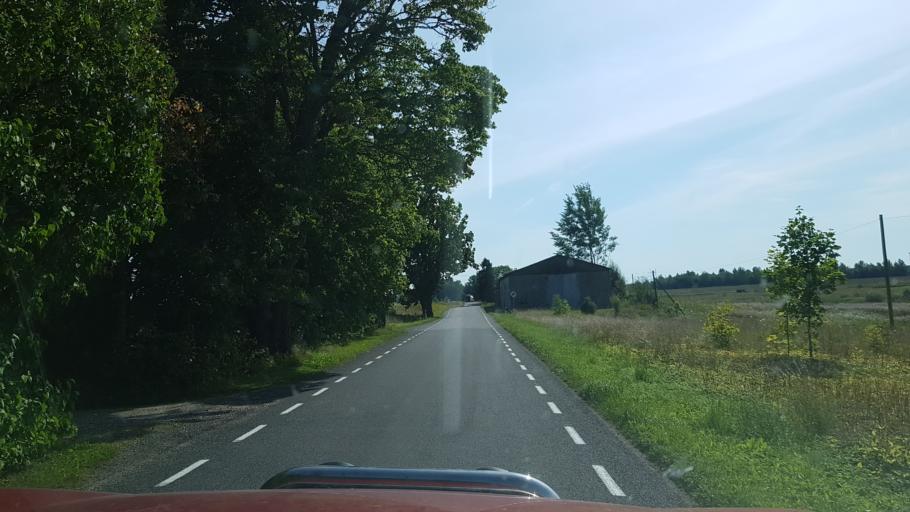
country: EE
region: Viljandimaa
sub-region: Viljandi linn
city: Viljandi
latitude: 58.3938
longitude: 25.6083
